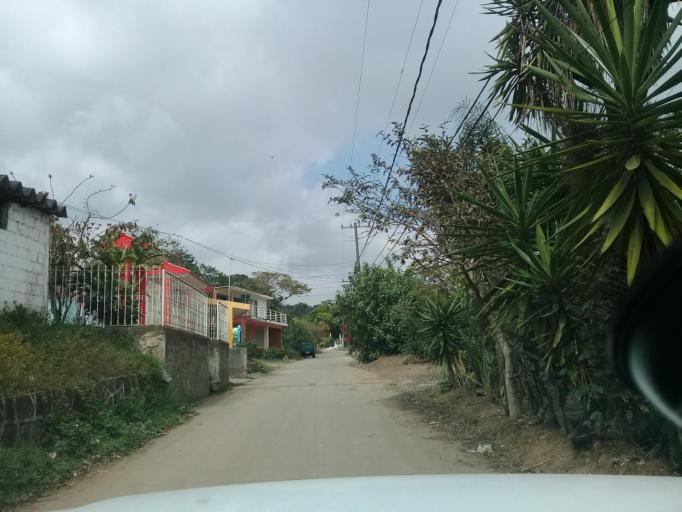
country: MX
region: Veracruz
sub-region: Xalapa
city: Fraccionamiento las Fuentes
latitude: 19.4780
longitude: -96.8756
